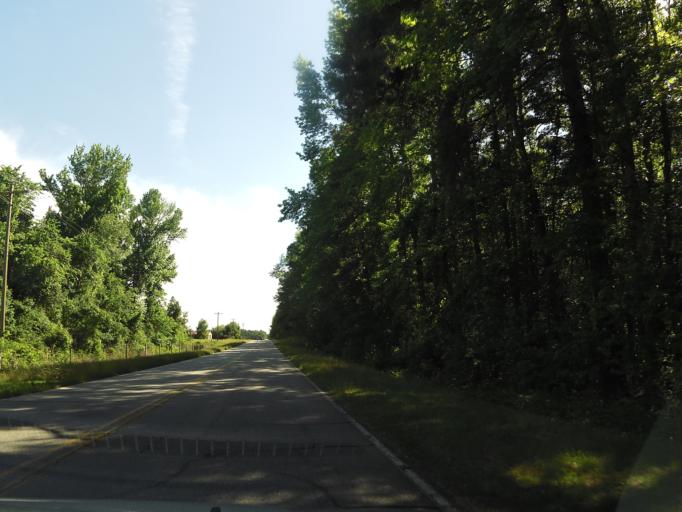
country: US
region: South Carolina
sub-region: Bamberg County
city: Denmark
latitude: 33.2473
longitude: -81.1647
